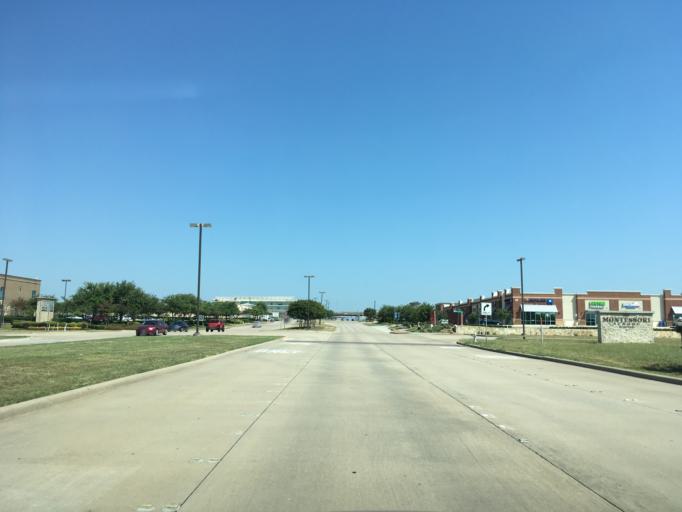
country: US
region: Texas
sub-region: Collin County
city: Allen
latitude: 33.1406
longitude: -96.6768
